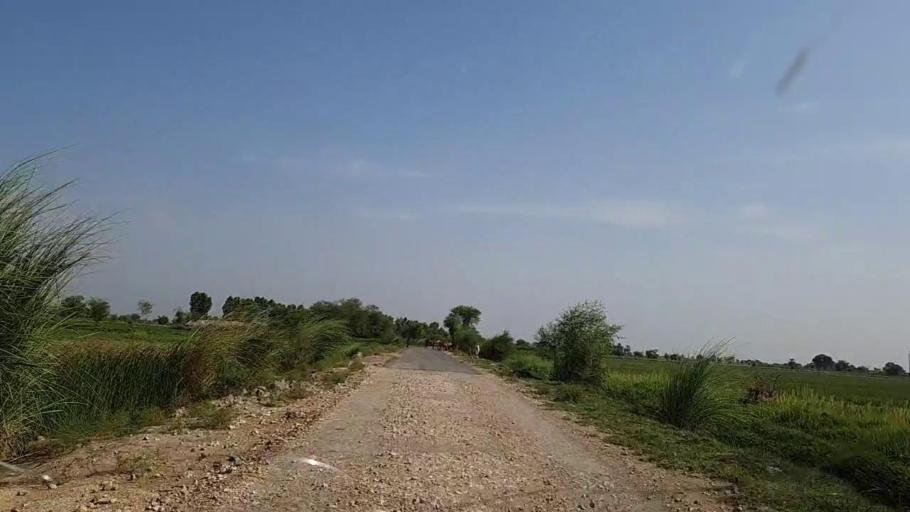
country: PK
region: Sindh
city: Khanpur
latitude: 27.7025
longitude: 69.3636
